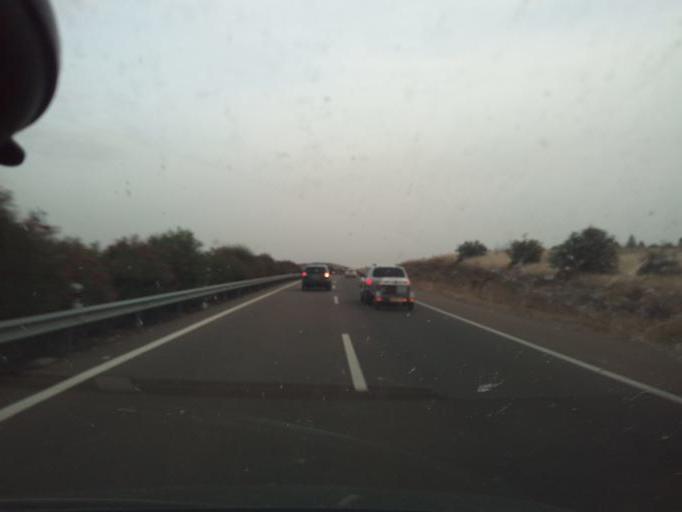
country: ES
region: Extremadura
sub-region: Provincia de Badajoz
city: Merida
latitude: 38.9448
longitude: -6.3074
